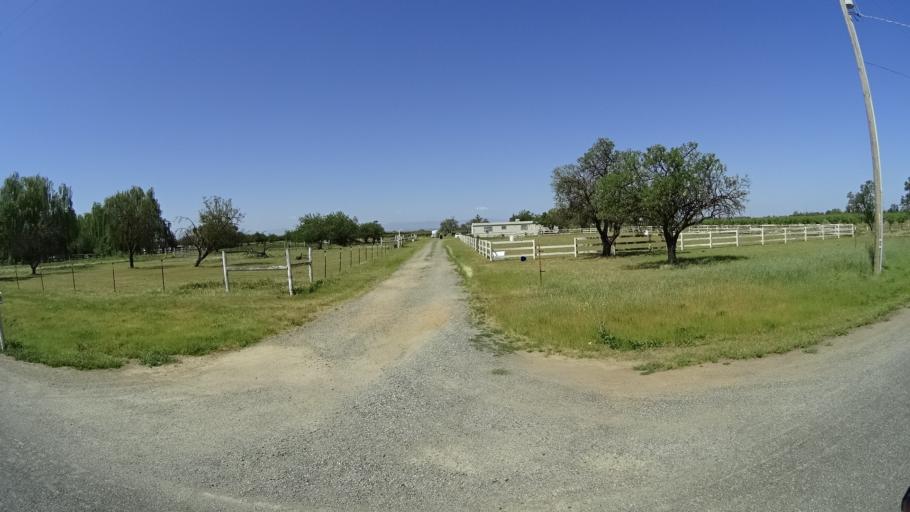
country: US
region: California
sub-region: Glenn County
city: Orland
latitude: 39.7828
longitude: -122.1595
